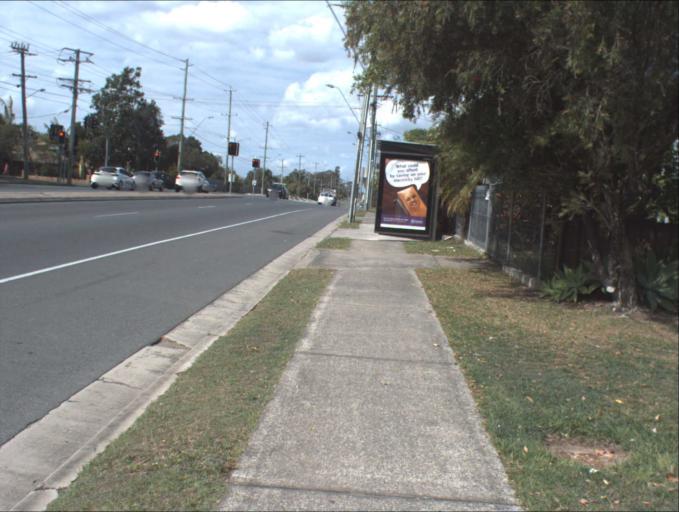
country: AU
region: Queensland
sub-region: Logan
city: Waterford West
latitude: -27.6813
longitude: 153.0922
